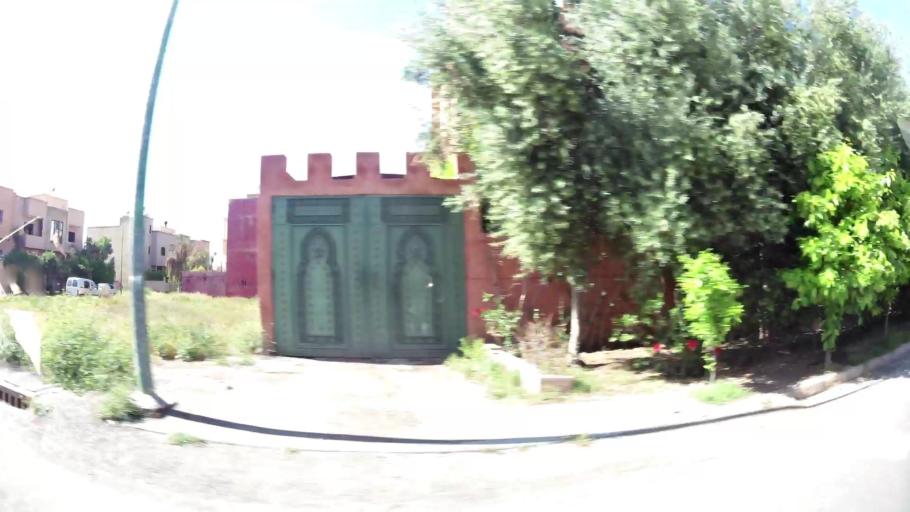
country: MA
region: Marrakech-Tensift-Al Haouz
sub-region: Marrakech
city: Marrakesh
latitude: 31.6380
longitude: -8.0423
